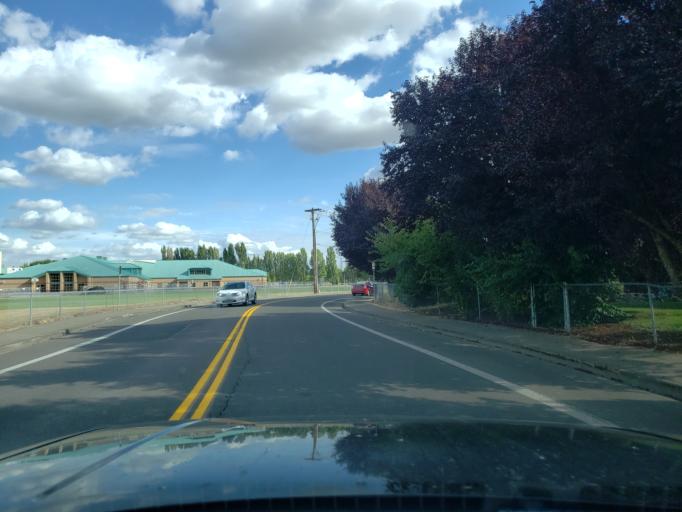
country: US
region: Oregon
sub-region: Yamhill County
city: McMinnville
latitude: 45.2012
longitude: -123.2195
